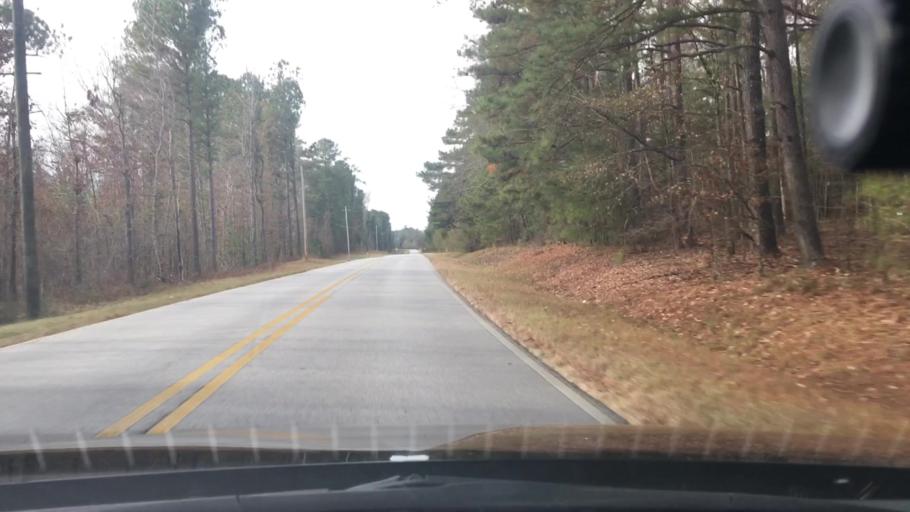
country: US
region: Georgia
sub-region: Spalding County
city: Experiment
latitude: 33.2696
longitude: -84.3426
